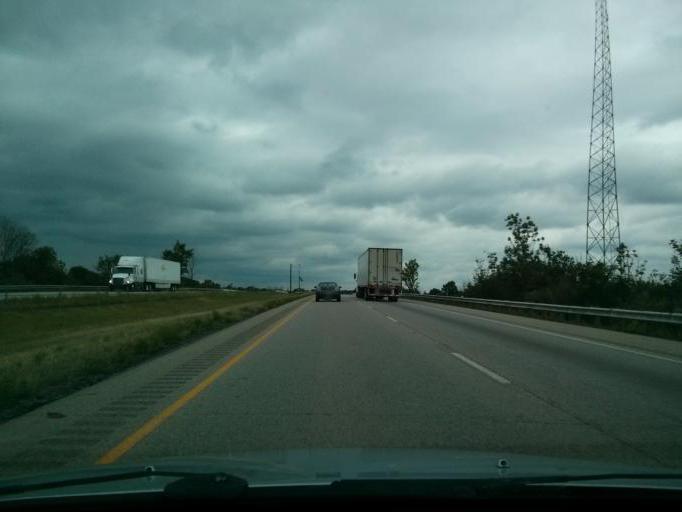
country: US
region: Ohio
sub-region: Mahoning County
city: Craig Beach
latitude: 41.1017
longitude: -81.0247
